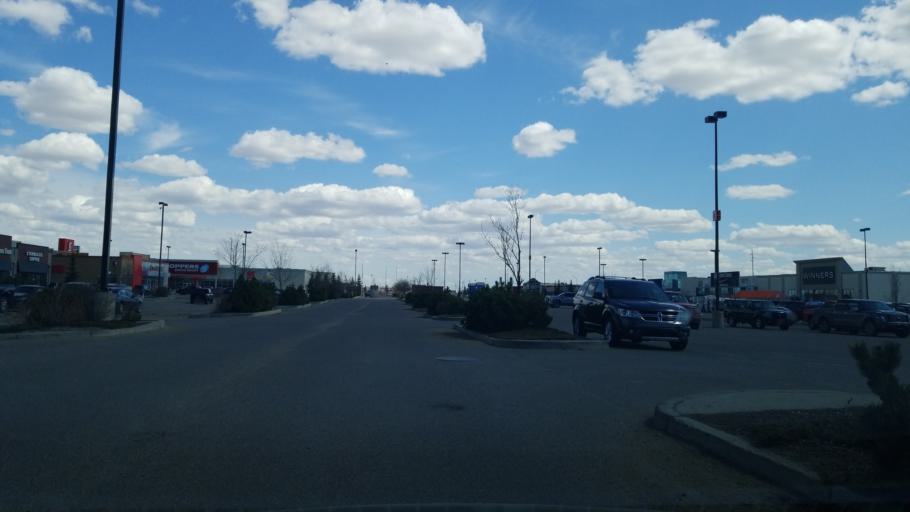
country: CA
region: Saskatchewan
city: Lloydminster
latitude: 53.2770
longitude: -110.0590
